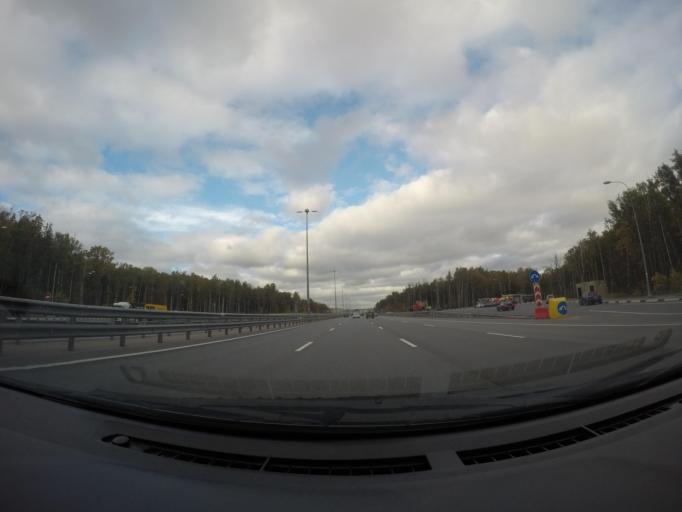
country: RU
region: Moskovskaya
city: Nemchinovka
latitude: 55.7162
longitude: 37.3200
